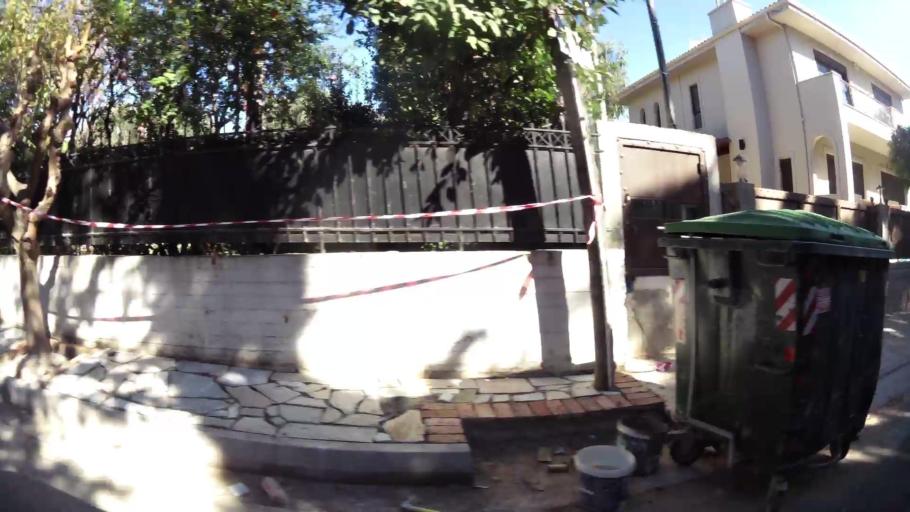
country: GR
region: Attica
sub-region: Nomarchia Anatolikis Attikis
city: Pikermi
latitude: 38.0050
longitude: 23.9391
